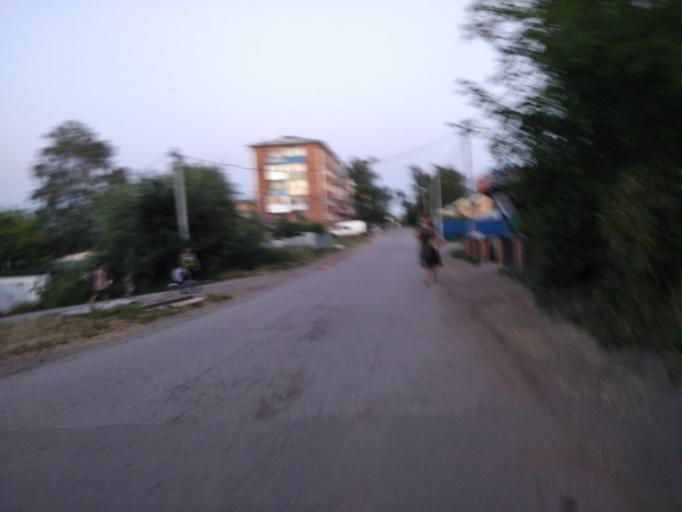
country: RU
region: Tula
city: Lomintsevskiy
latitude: 53.9365
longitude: 37.6293
